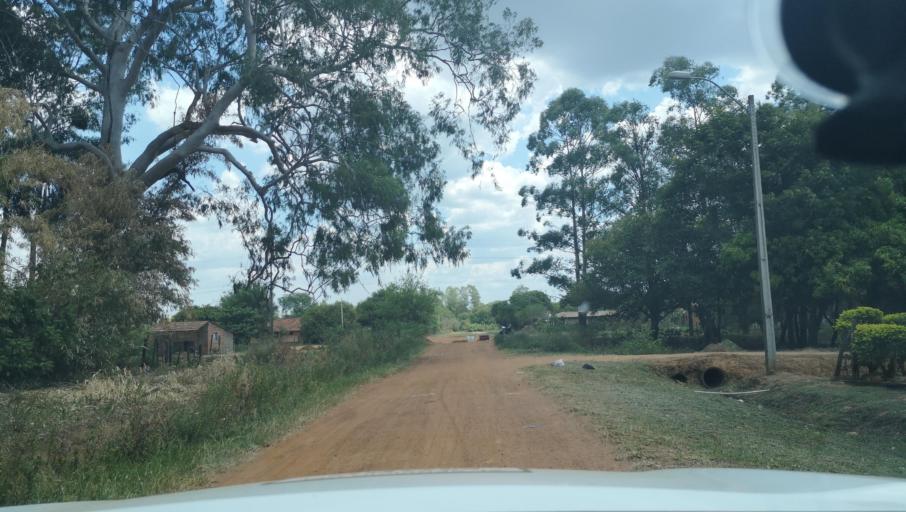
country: PY
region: Itapua
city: Carmen del Parana
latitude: -27.1720
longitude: -56.2388
